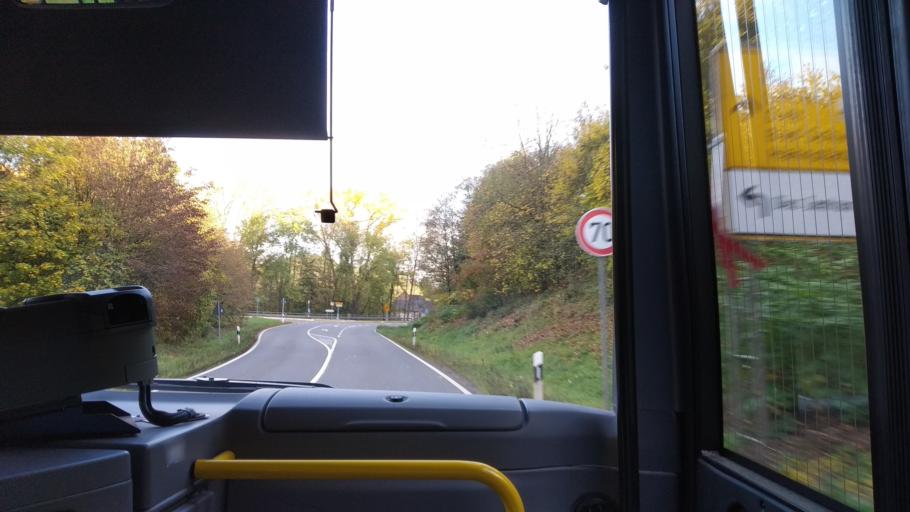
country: DE
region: Rheinland-Pfalz
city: Diez
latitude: 50.3635
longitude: 8.0285
